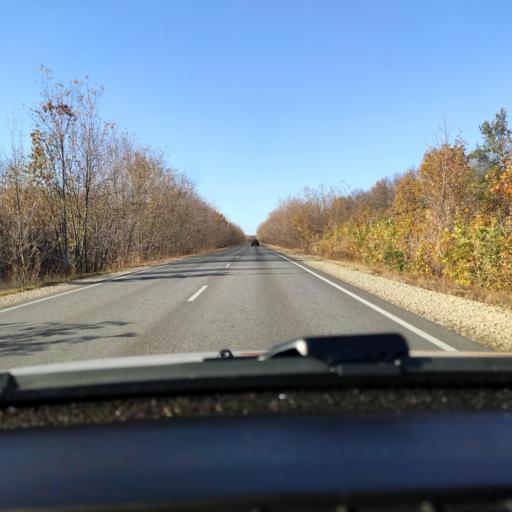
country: RU
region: Voronezj
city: Zemlyansk
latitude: 51.8430
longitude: 38.8078
